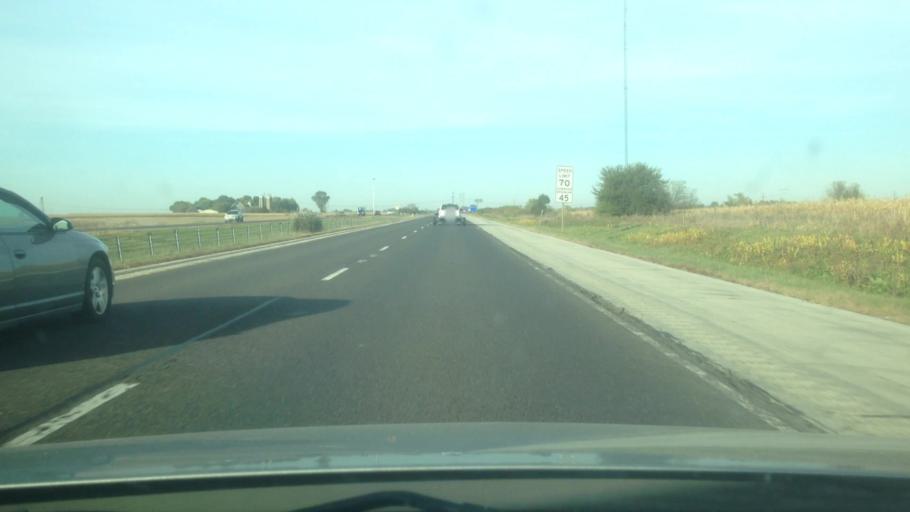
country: US
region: Illinois
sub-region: Kankakee County
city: Manteno
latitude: 41.2973
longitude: -87.8293
